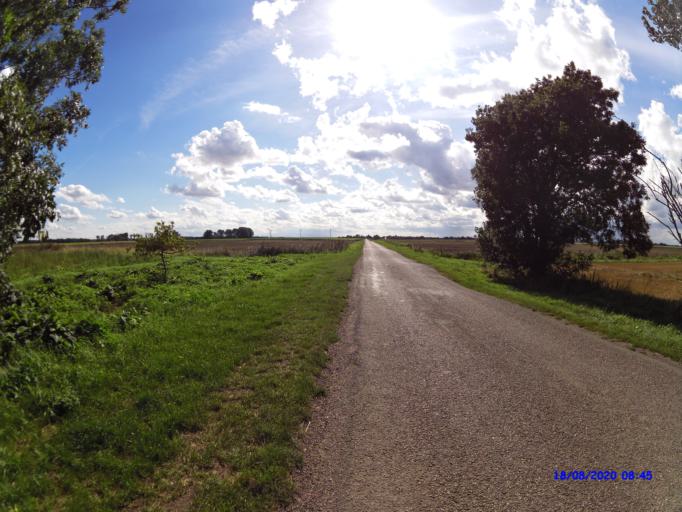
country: GB
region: England
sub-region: Cambridgeshire
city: Ramsey
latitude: 52.4895
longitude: -0.0890
